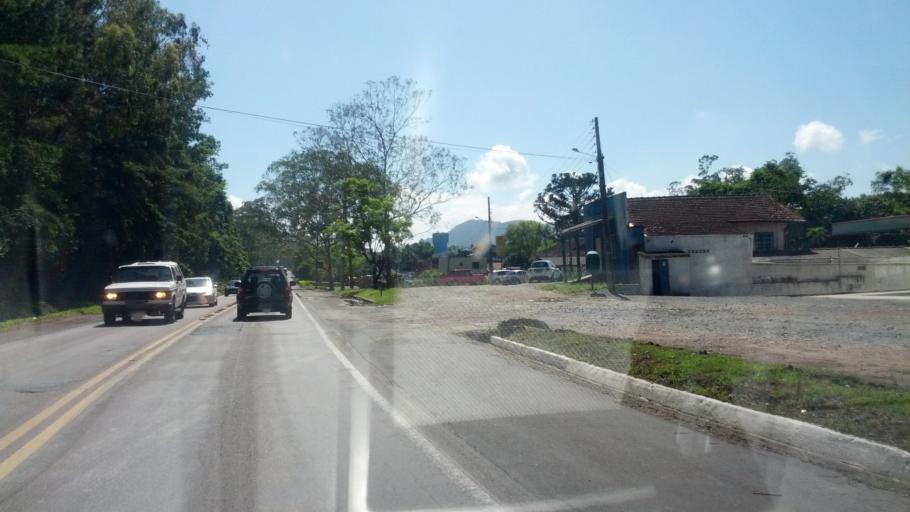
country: BR
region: Santa Catarina
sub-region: Rio Do Sul
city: Rio do Sul
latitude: -27.1893
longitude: -49.6181
